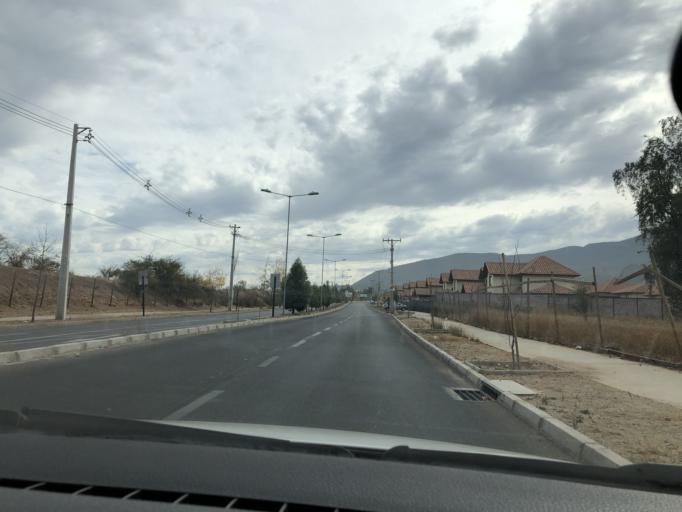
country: CL
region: Santiago Metropolitan
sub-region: Provincia de Cordillera
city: Puente Alto
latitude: -33.5920
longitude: -70.5074
